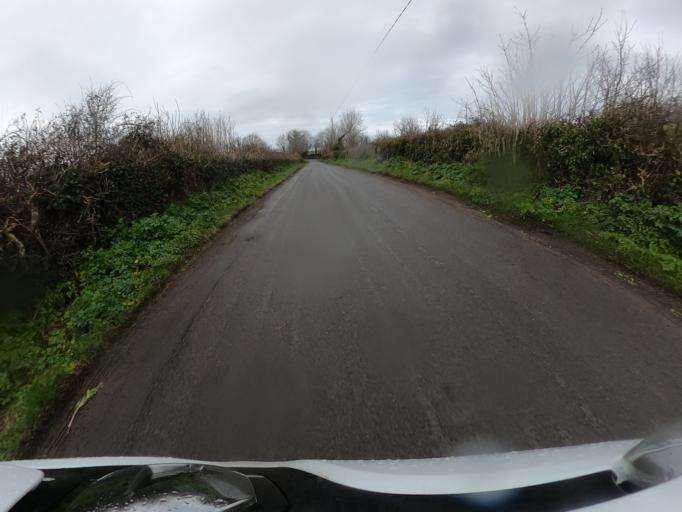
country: IM
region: Ramsey
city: Ramsey
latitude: 54.3770
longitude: -4.4535
